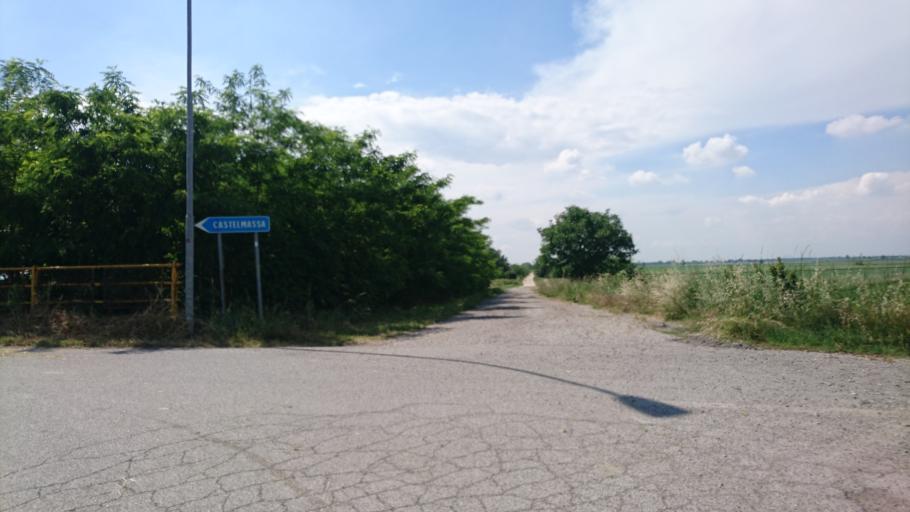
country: IT
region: Veneto
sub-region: Provincia di Rovigo
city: Castelmassa
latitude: 45.0744
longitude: 11.3392
